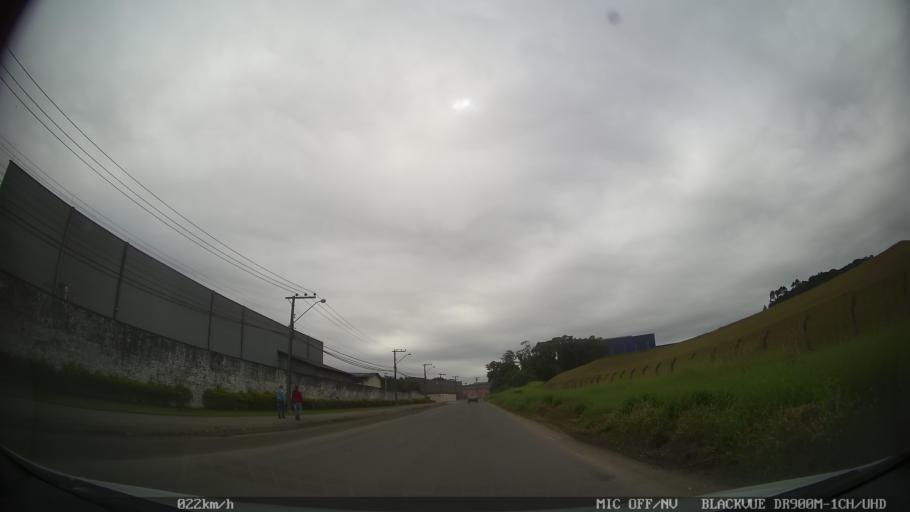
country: BR
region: Santa Catarina
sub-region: Joinville
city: Joinville
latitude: -26.2633
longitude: -48.8838
